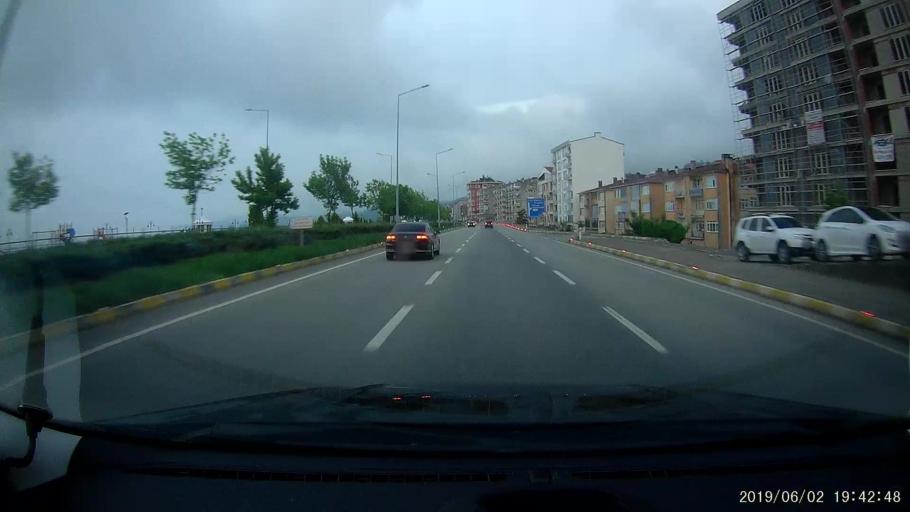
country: TR
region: Giresun
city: Kesap
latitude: 40.9170
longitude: 38.5128
